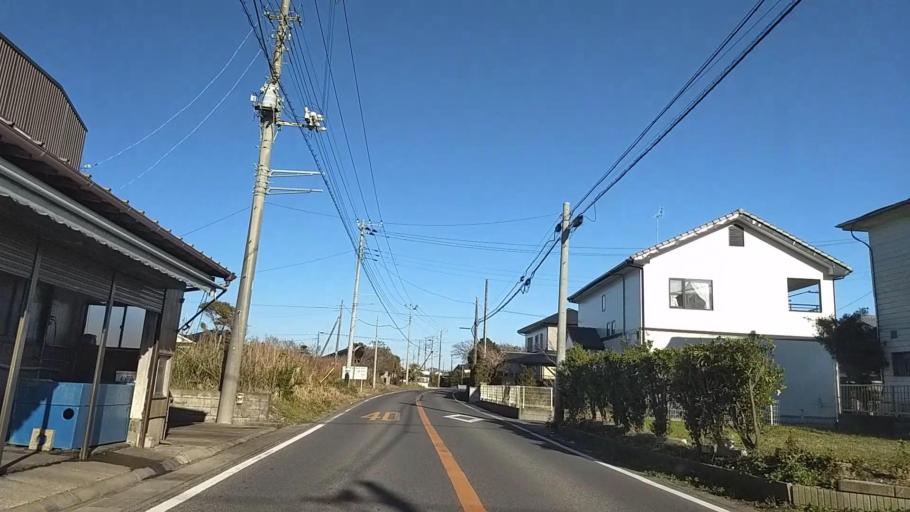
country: JP
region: Chiba
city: Yokaichiba
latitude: 35.6232
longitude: 140.5457
